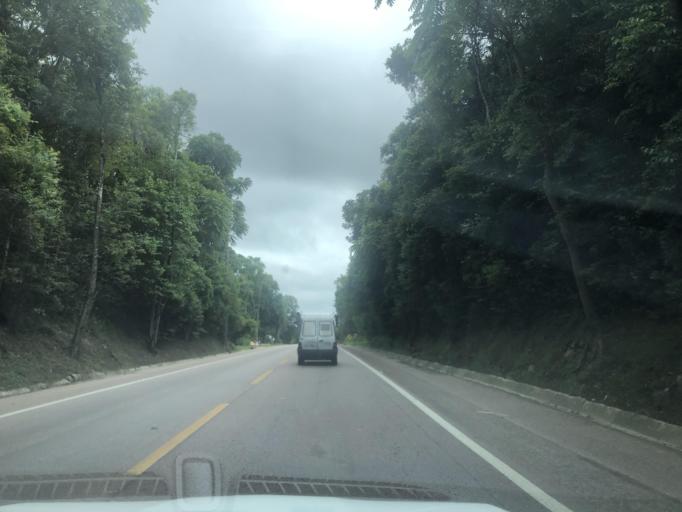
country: BR
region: Parana
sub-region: Araucaria
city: Araucaria
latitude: -25.8413
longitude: -49.3462
